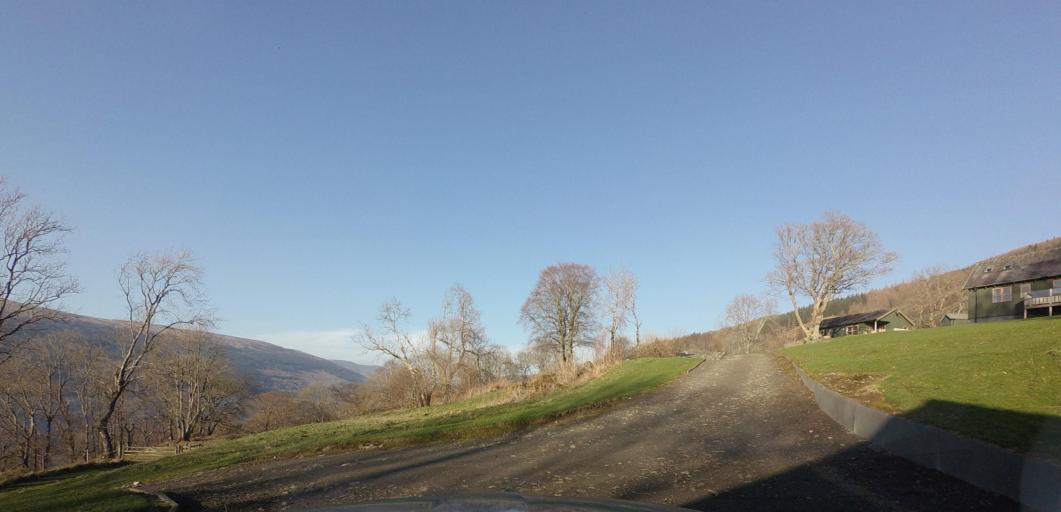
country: GB
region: Scotland
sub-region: Perth and Kinross
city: Comrie
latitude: 56.5397
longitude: -4.1050
